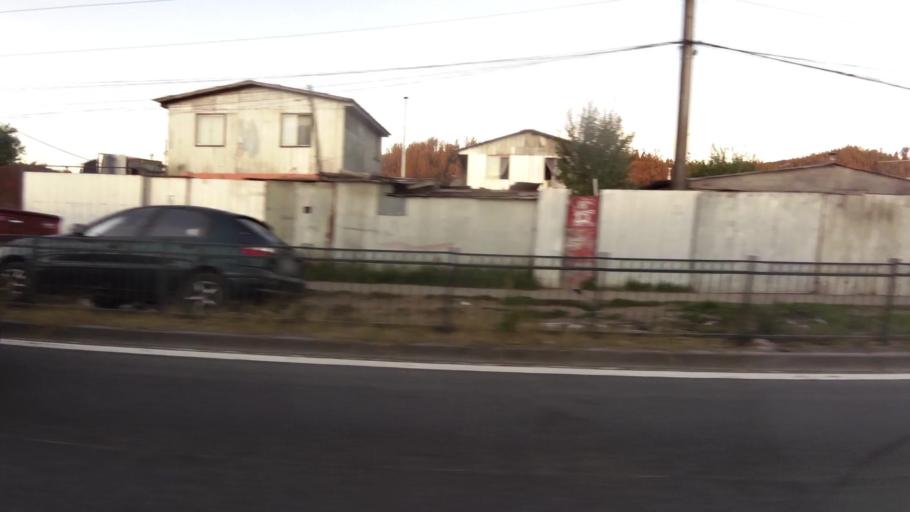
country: CL
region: Biobio
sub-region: Provincia de Concepcion
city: Concepcion
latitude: -36.8423
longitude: -73.0579
